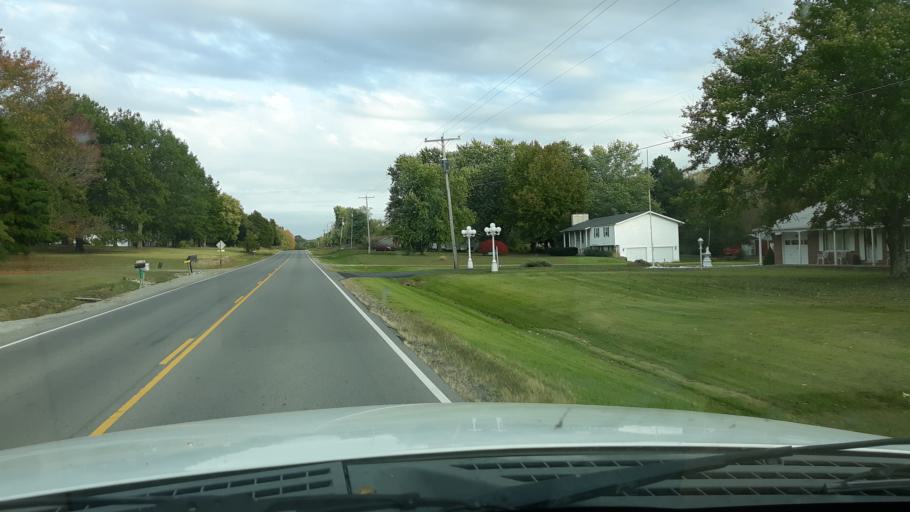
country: US
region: Illinois
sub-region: Saline County
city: Eldorado
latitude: 37.8236
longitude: -88.5020
